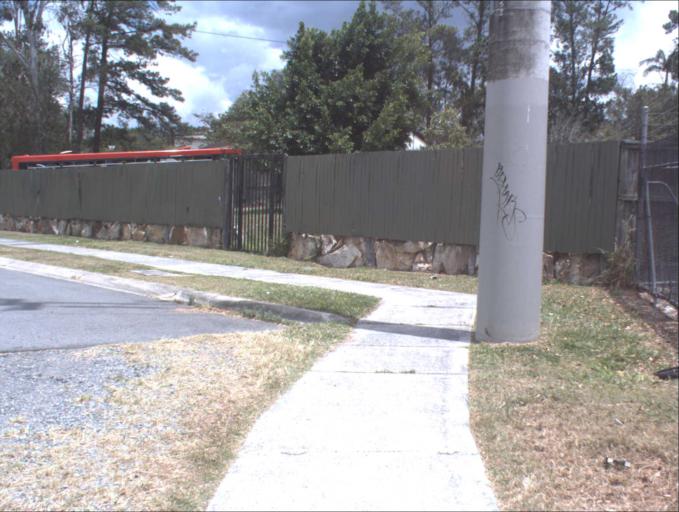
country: AU
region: Queensland
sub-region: Gold Coast
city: Yatala
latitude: -27.7208
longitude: 153.2076
